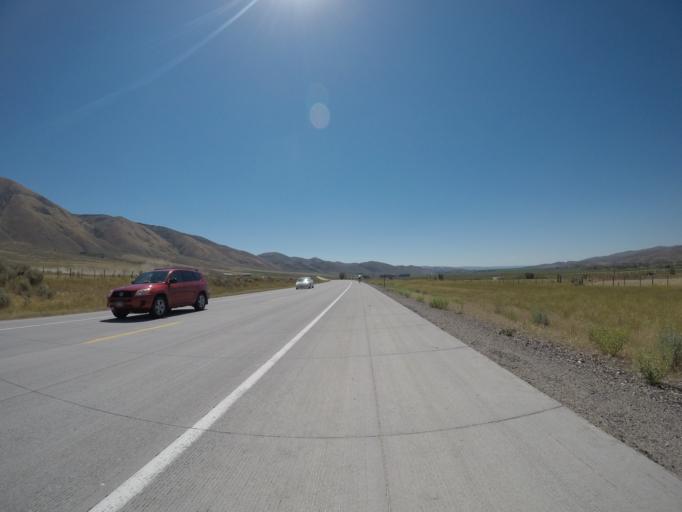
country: US
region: Idaho
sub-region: Bear Lake County
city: Montpelier
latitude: 42.1806
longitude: -111.0081
